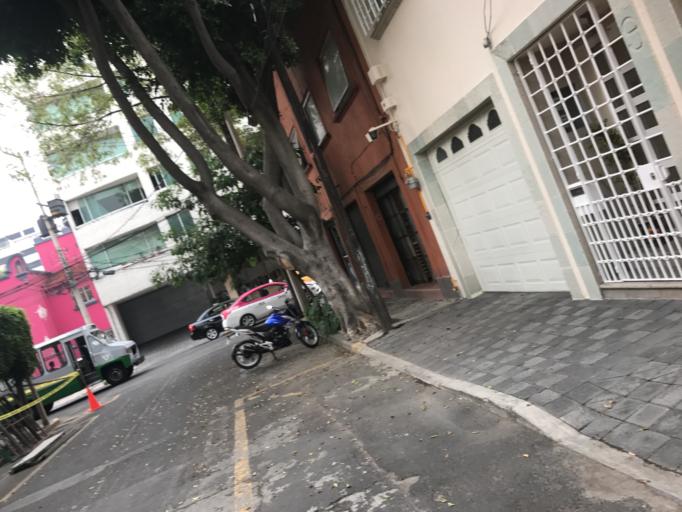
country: MX
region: Mexico City
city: Coyoacan
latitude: 19.3648
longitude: -99.1788
